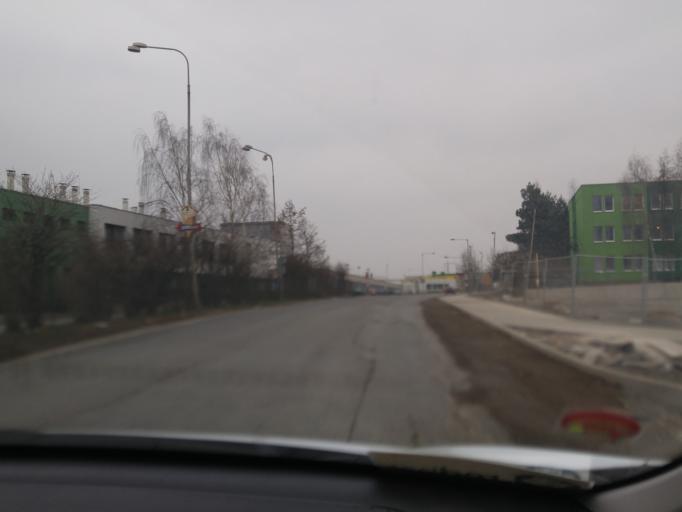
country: CZ
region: Central Bohemia
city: Brandys nad Labem-Stara Boleslav
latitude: 50.1793
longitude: 14.6691
